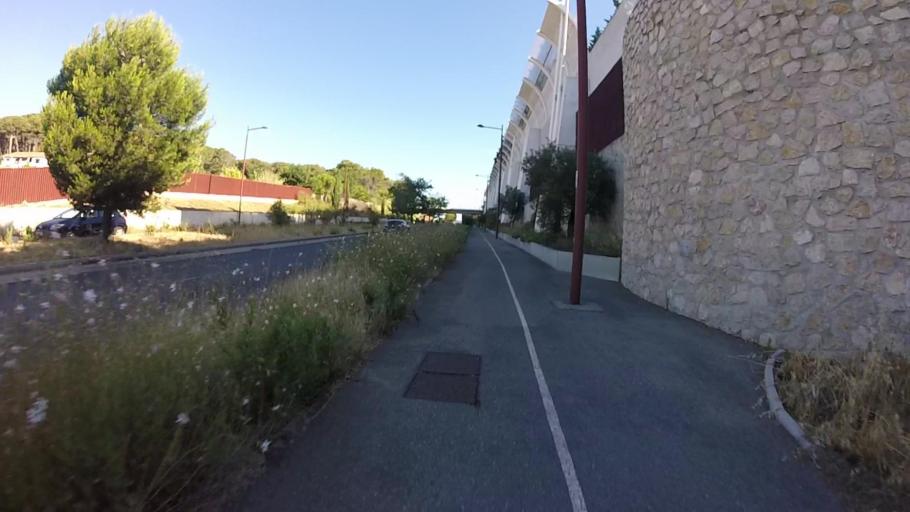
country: FR
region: Provence-Alpes-Cote d'Azur
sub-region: Departement des Alpes-Maritimes
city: Biot
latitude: 43.5921
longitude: 7.0922
